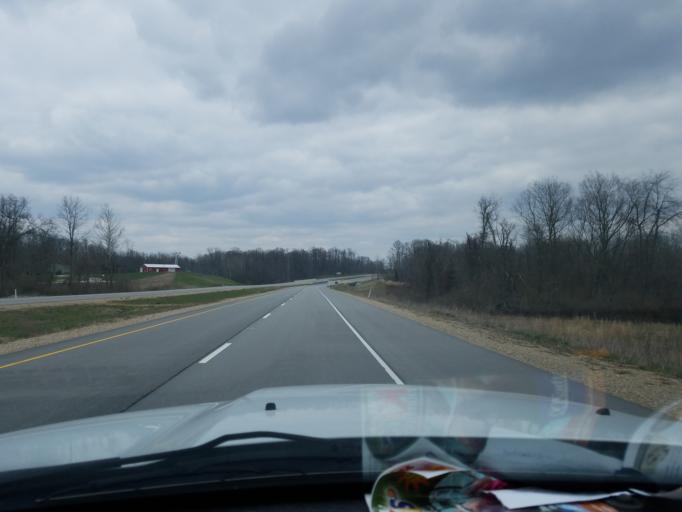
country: US
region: Indiana
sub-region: Vigo County
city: Terre Haute
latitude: 39.4077
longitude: -87.3641
